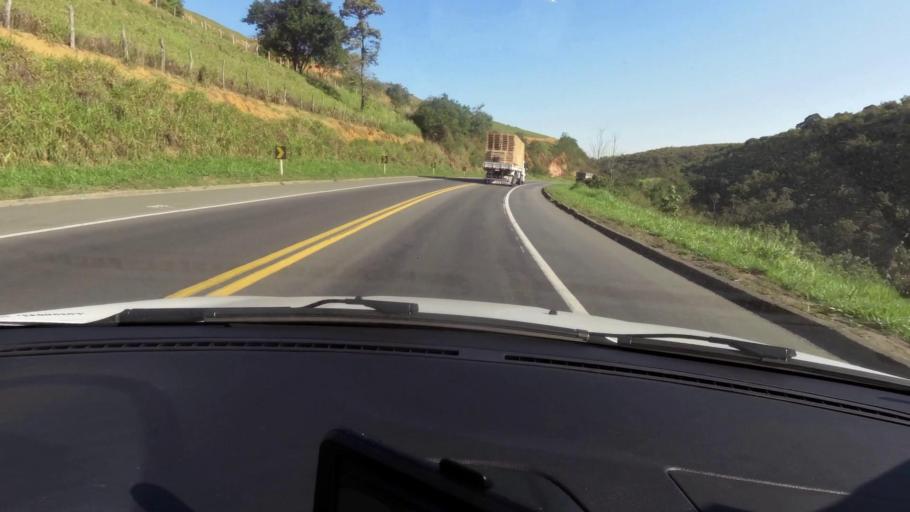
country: BR
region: Espirito Santo
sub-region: Alfredo Chaves
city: Alfredo Chaves
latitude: -20.6750
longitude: -40.6647
